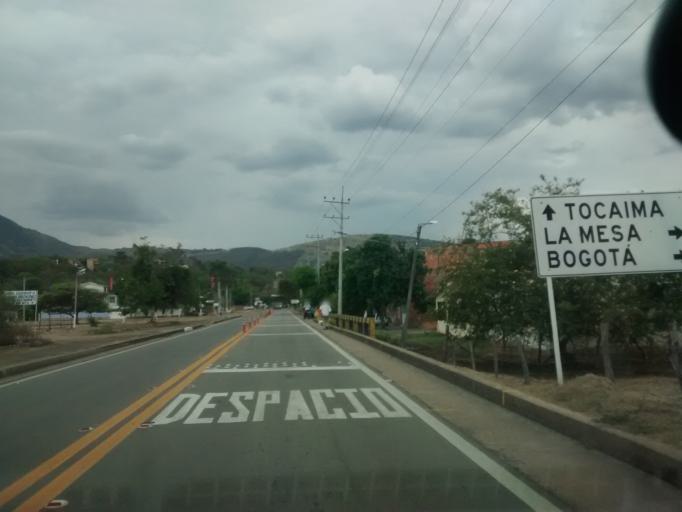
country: CO
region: Cundinamarca
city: Tocaima
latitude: 4.4545
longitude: -74.6458
